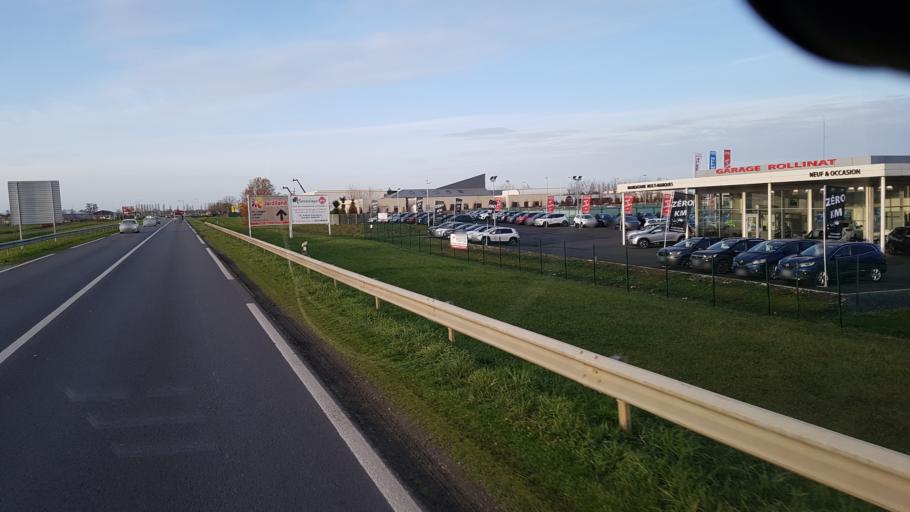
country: FR
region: Centre
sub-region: Departement de l'Indre
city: Chateauroux
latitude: 46.7906
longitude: 1.7093
